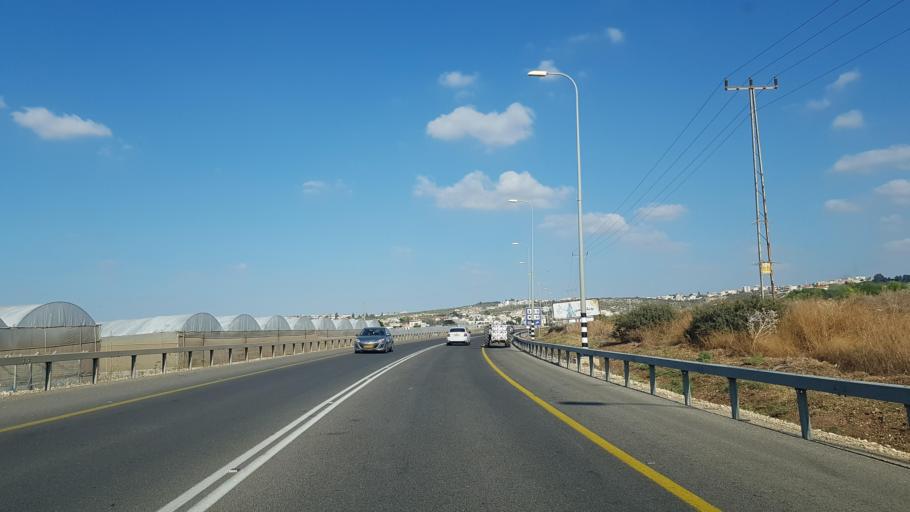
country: PS
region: West Bank
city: Zayta
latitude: 32.3581
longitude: 35.0191
